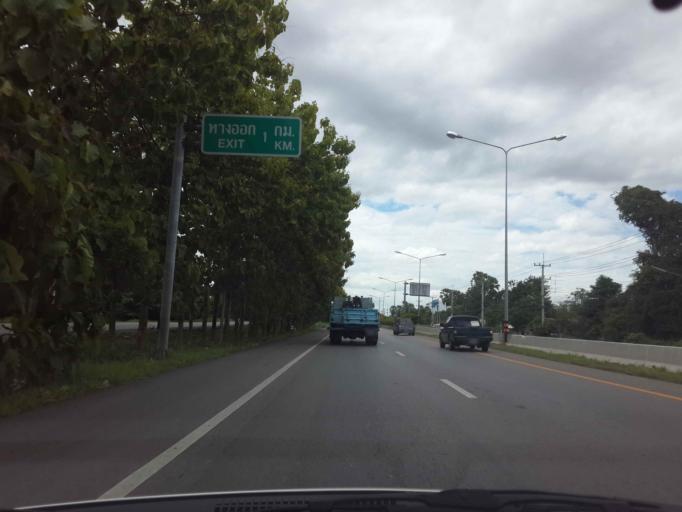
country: TH
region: Phetchaburi
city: Khao Yoi
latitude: 13.1514
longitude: 99.8517
